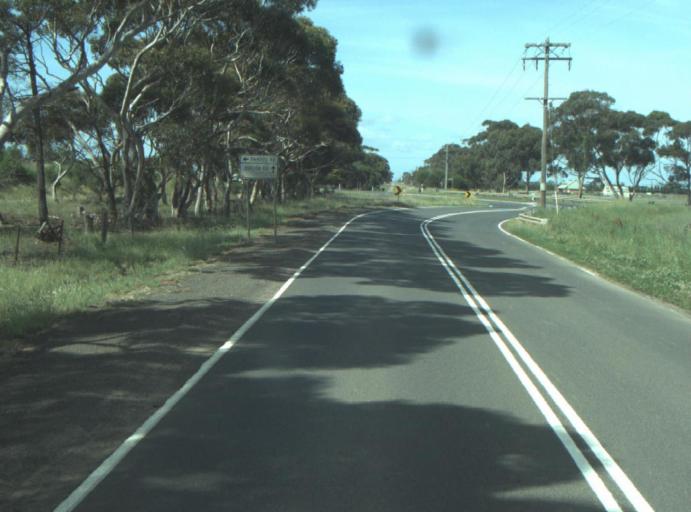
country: AU
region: Victoria
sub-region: Greater Geelong
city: Lara
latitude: -38.0543
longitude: 144.4279
